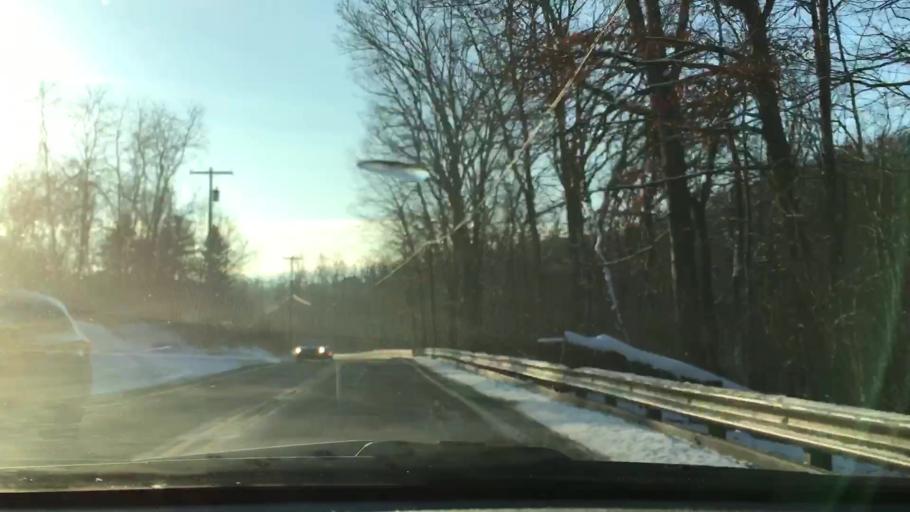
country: US
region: Pennsylvania
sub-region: Allegheny County
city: Elizabeth
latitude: 40.2623
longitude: -79.8517
